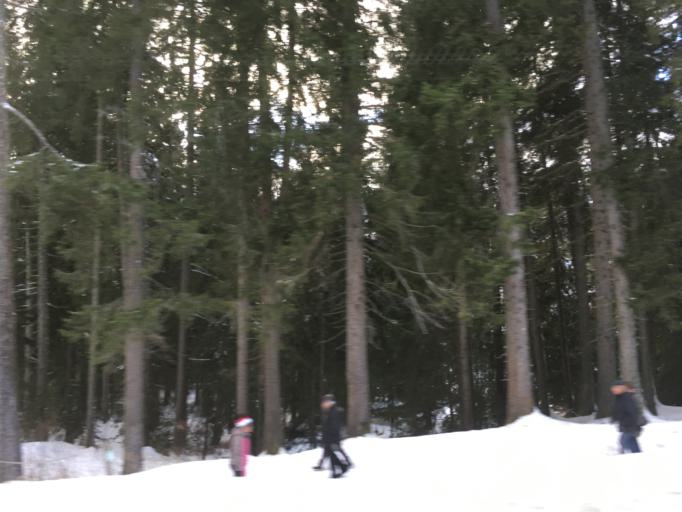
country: CH
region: Grisons
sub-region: Plessur District
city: Churwalden
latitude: 46.7343
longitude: 9.5518
